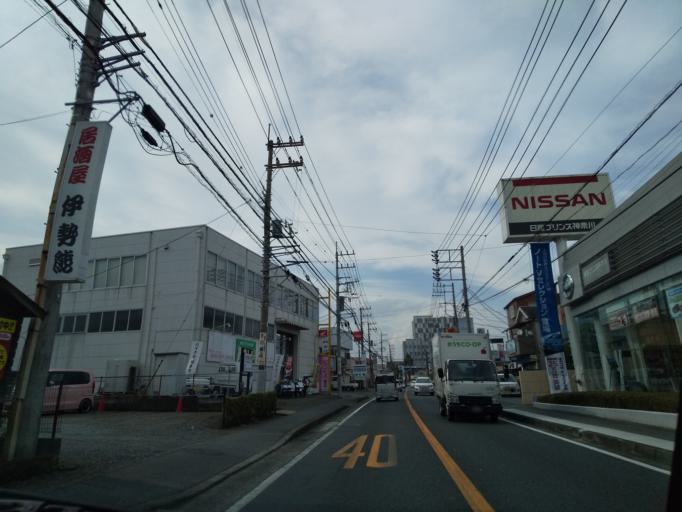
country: JP
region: Kanagawa
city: Atsugi
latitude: 35.4821
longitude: 139.3413
